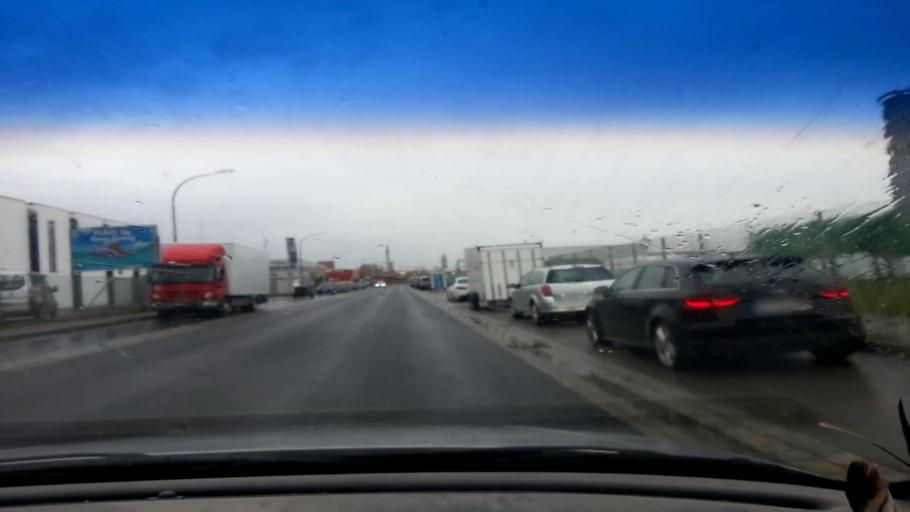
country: DE
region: Bavaria
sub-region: Upper Franconia
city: Hallstadt
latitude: 49.9080
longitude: 10.8748
